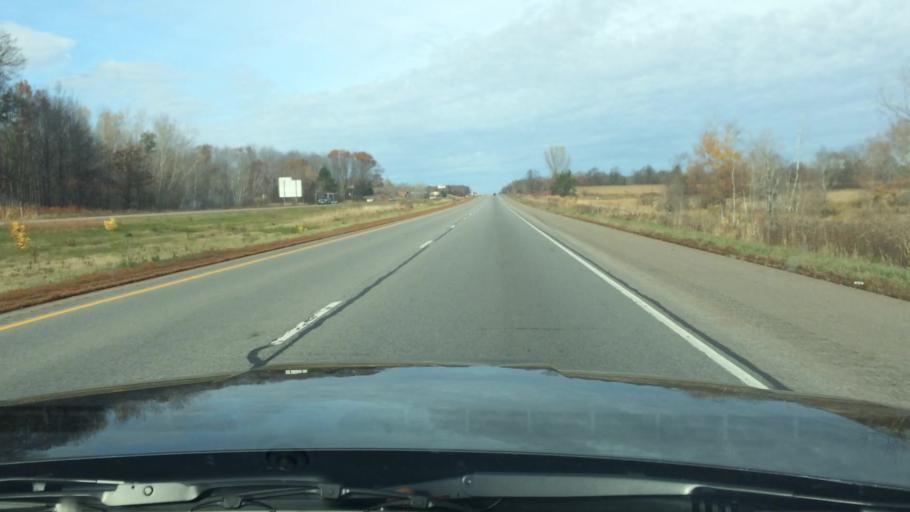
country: US
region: Wisconsin
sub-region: Marathon County
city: Mosinee
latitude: 44.7473
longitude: -89.6797
